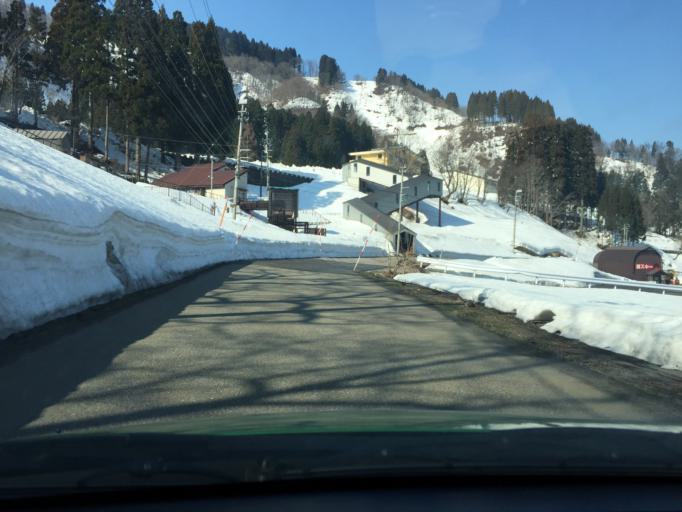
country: JP
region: Ishikawa
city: Tsurugi-asahimachi
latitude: 36.2692
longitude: 136.7122
